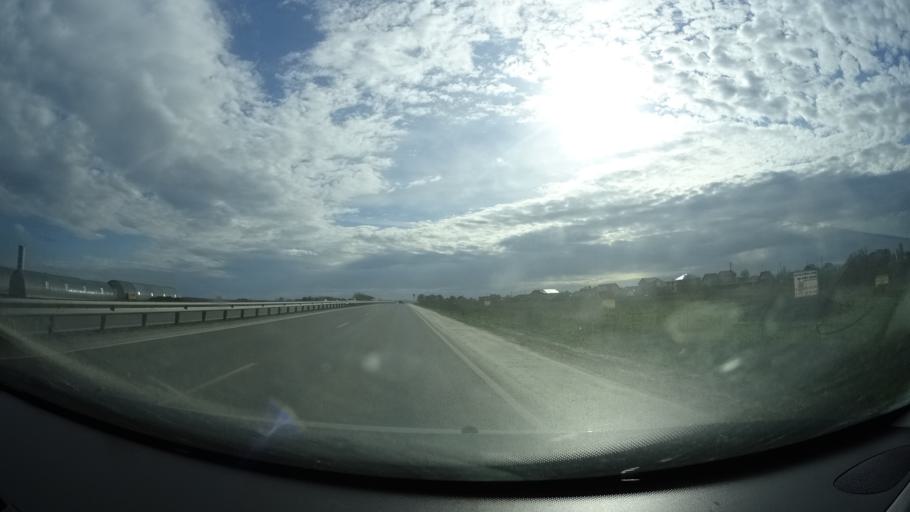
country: RU
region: Perm
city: Kultayevo
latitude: 57.9037
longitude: 55.9808
